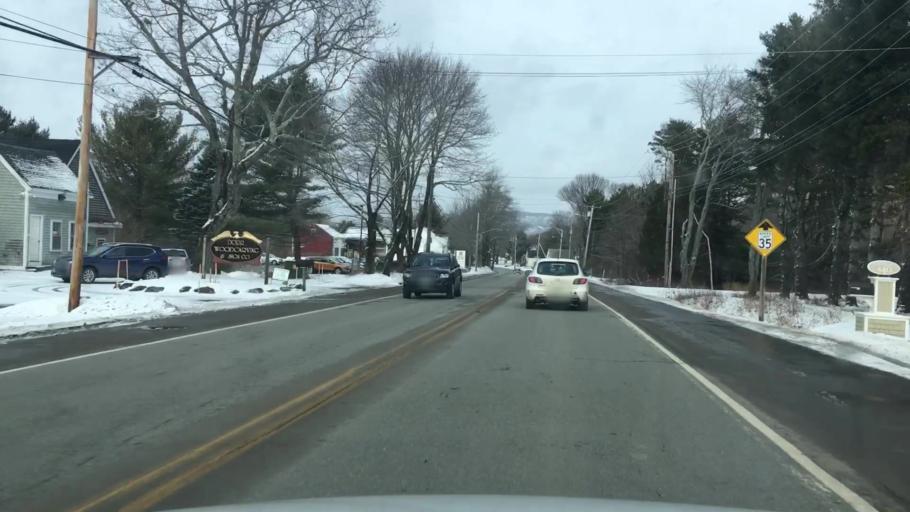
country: US
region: Maine
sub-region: Knox County
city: Rockport
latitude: 44.1716
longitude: -69.0799
